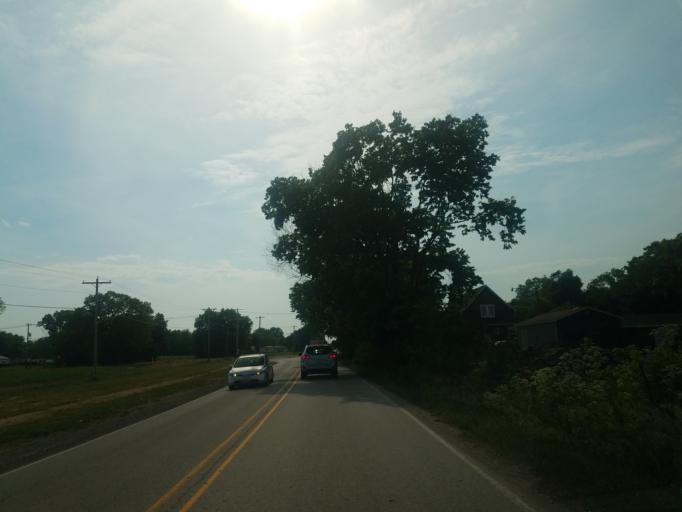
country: US
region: Illinois
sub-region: McLean County
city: Bloomington
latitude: 40.4514
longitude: -88.9800
